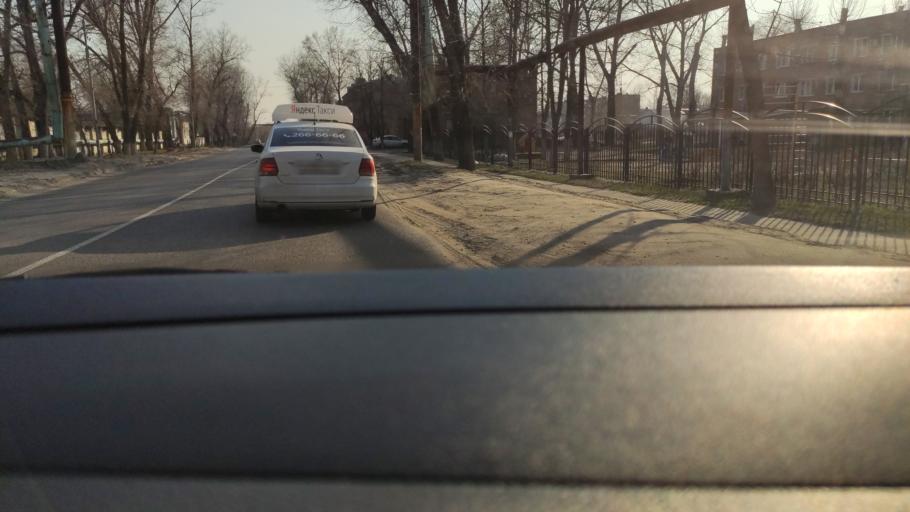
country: RU
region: Voronezj
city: Maslovka
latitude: 51.5818
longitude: 39.3168
